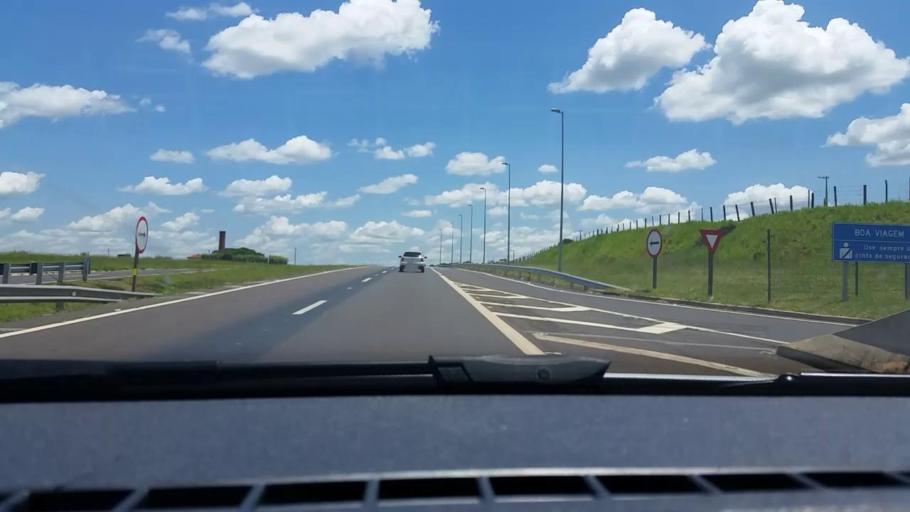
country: BR
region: Sao Paulo
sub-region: Bauru
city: Bauru
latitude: -22.4410
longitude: -49.1479
